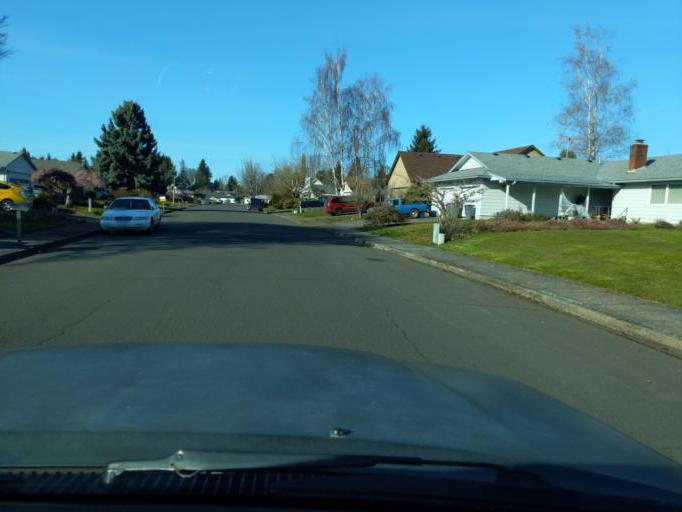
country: US
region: Oregon
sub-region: Yamhill County
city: McMinnville
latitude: 45.2001
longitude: -123.2116
